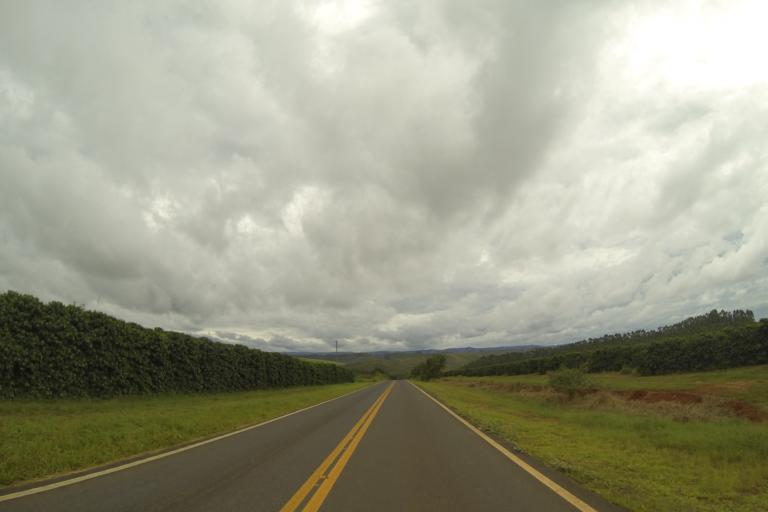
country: BR
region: Minas Gerais
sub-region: Bambui
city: Bambui
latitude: -20.0541
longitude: -46.1587
